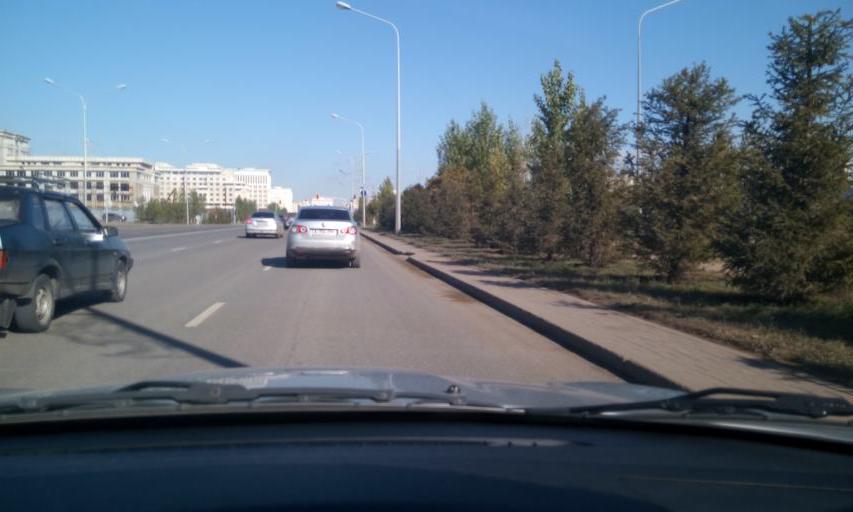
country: KZ
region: Astana Qalasy
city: Astana
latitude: 51.0983
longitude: 71.4280
